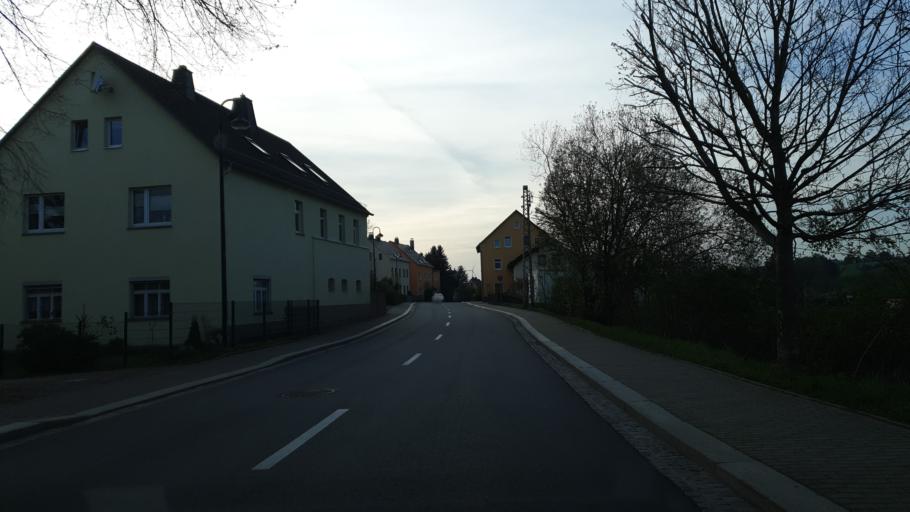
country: DE
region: Saxony
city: Gersdorf
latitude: 50.7420
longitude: 12.7299
